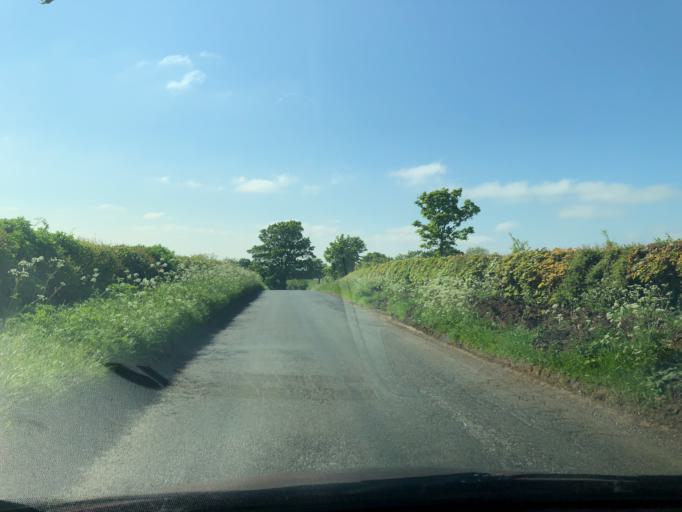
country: GB
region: England
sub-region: North Yorkshire
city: Northallerton
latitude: 54.3287
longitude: -1.4075
